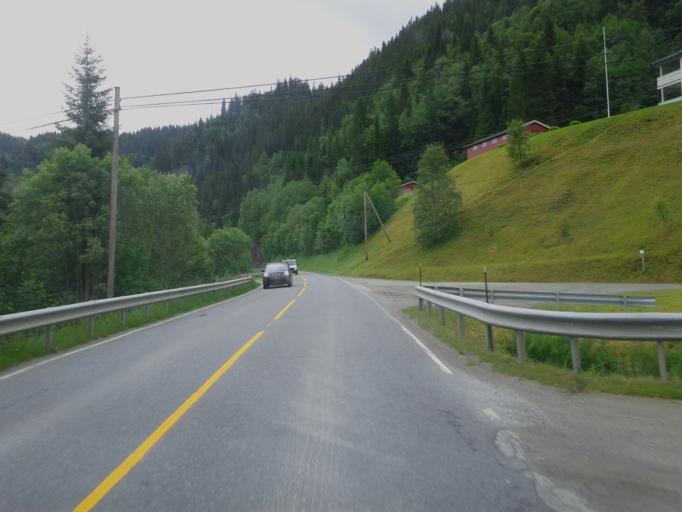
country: NO
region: Sor-Trondelag
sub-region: Midtre Gauldal
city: Storen
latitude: 62.9974
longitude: 10.4659
